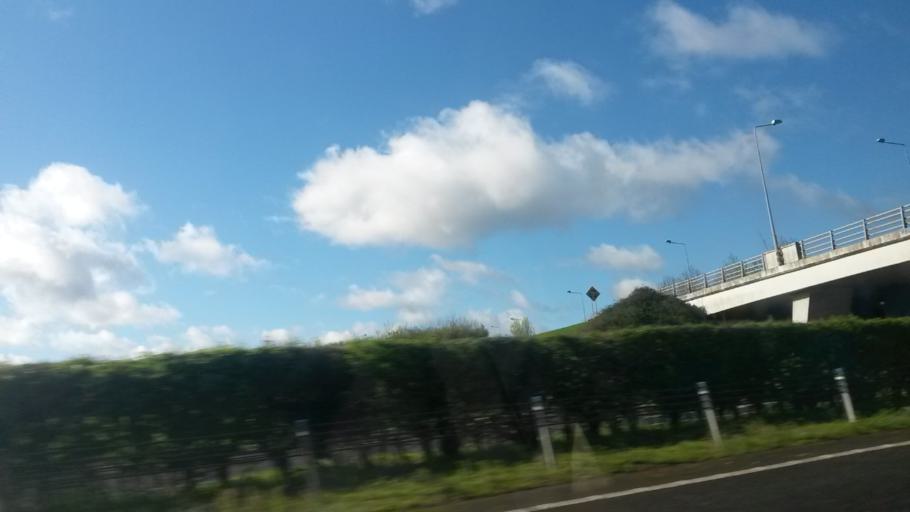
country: IE
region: Munster
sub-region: County Cork
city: Passage West
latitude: 51.9075
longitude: -8.3532
